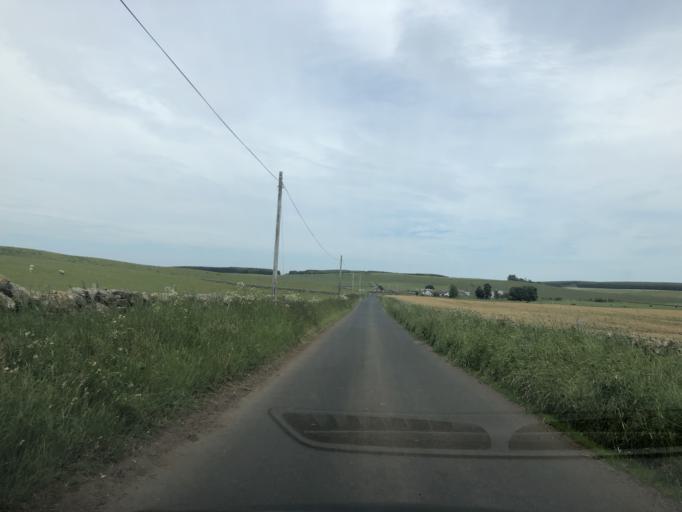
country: GB
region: Scotland
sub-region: The Scottish Borders
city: West Linton
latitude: 55.7602
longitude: -3.3367
